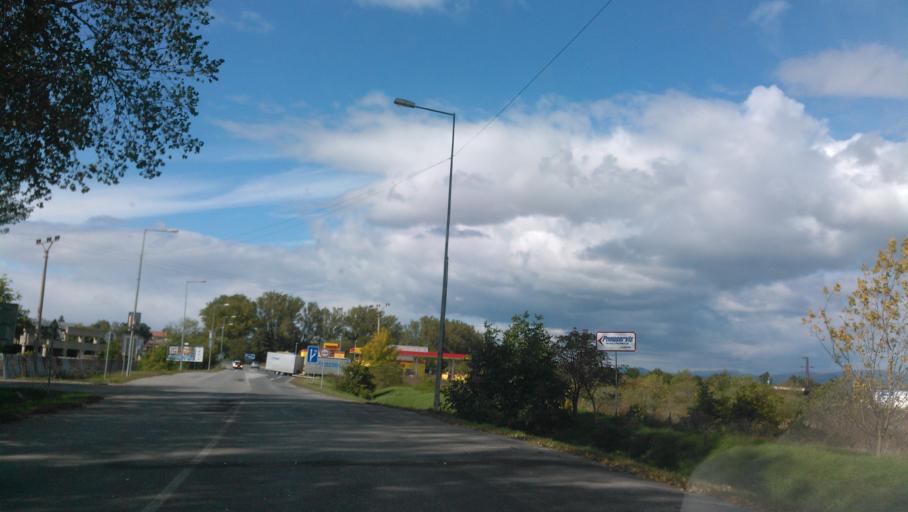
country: SK
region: Banskobystricky
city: Rimavska Sobota
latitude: 48.3872
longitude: 20.0002
